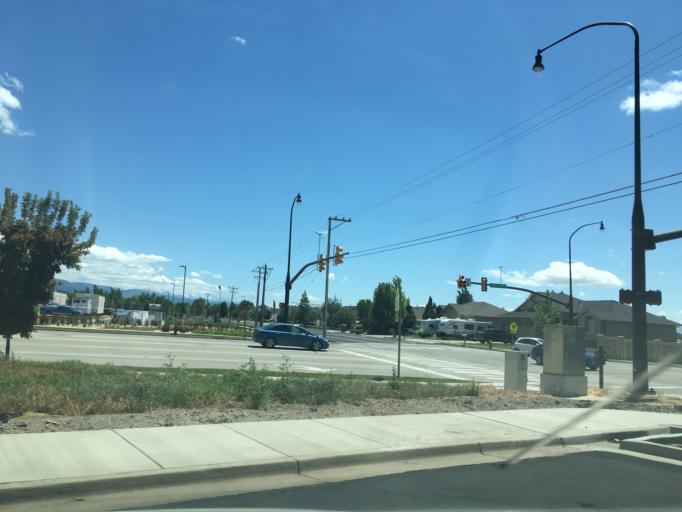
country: US
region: Utah
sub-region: Davis County
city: Layton
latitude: 41.0533
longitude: -111.9715
